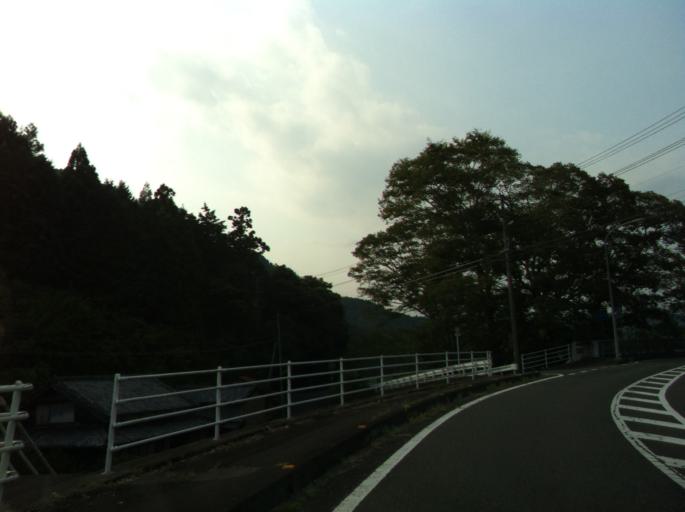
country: JP
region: Shizuoka
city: Fujieda
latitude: 34.9351
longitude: 138.2618
